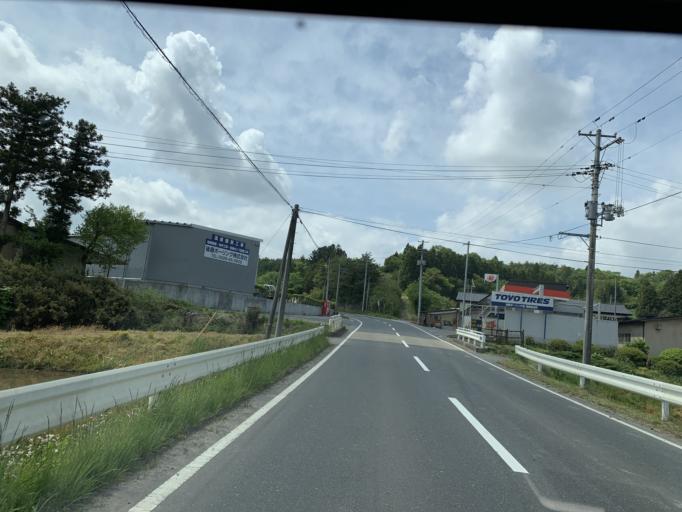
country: JP
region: Iwate
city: Ichinoseki
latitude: 38.7881
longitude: 141.0009
